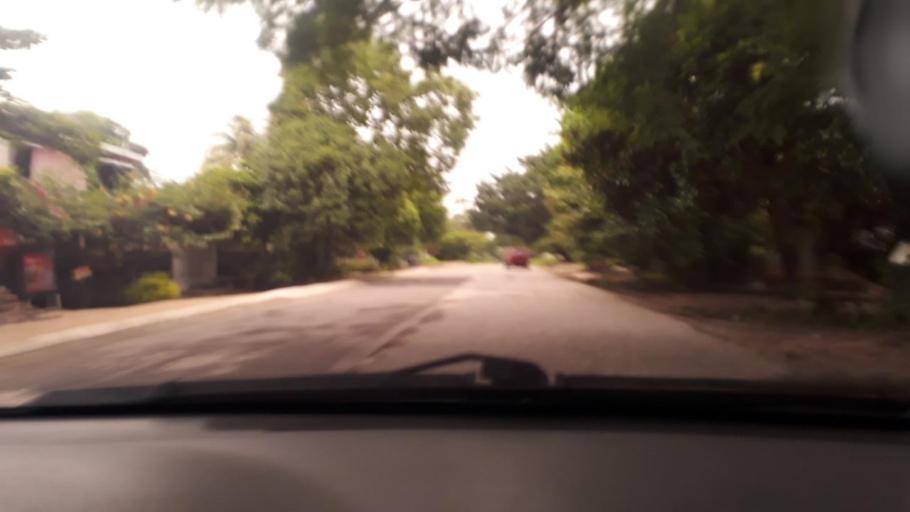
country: GT
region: Jutiapa
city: Jalpatagua
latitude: 14.1530
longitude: -90.0439
